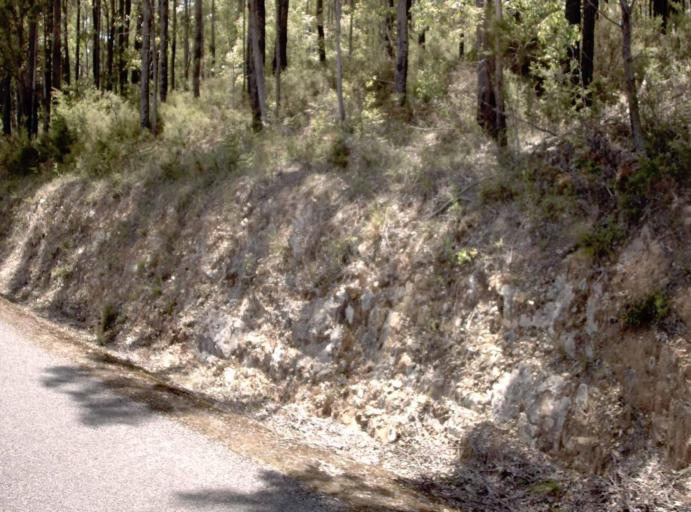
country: AU
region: New South Wales
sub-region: Bombala
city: Bombala
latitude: -37.5374
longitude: 148.9279
